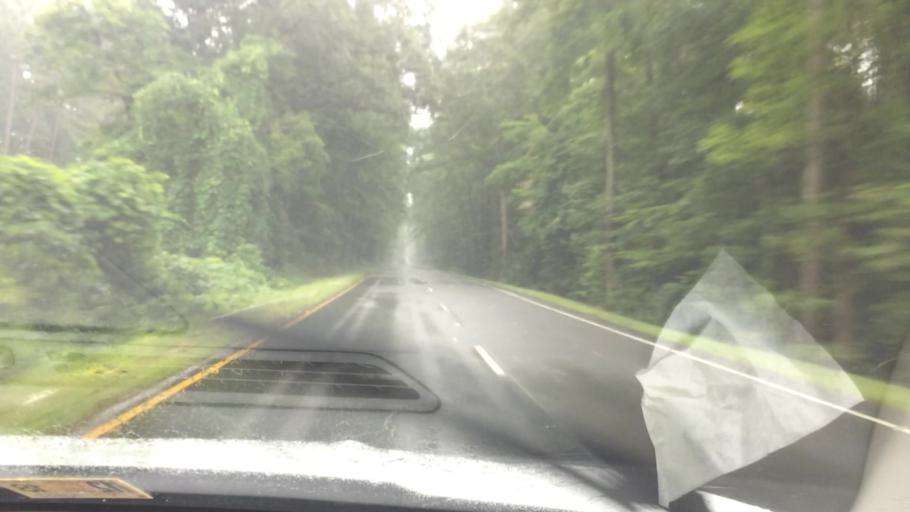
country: US
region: Virginia
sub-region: James City County
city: Williamsburg
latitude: 37.3947
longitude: -76.7807
